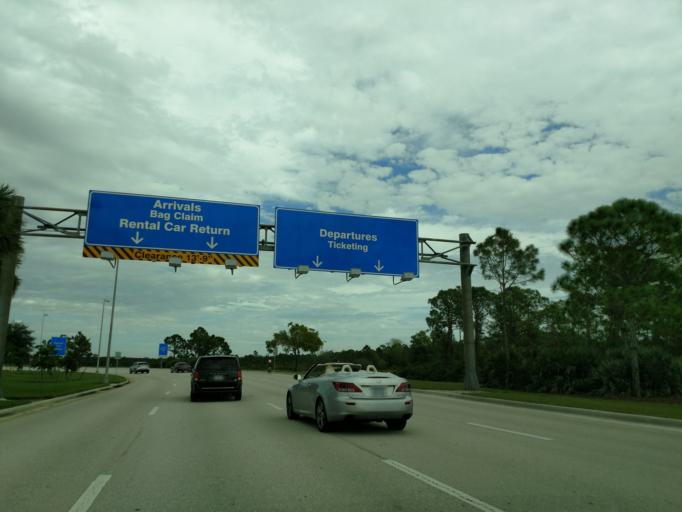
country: US
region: Florida
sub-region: Lee County
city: Gateway
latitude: 26.5228
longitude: -81.7531
